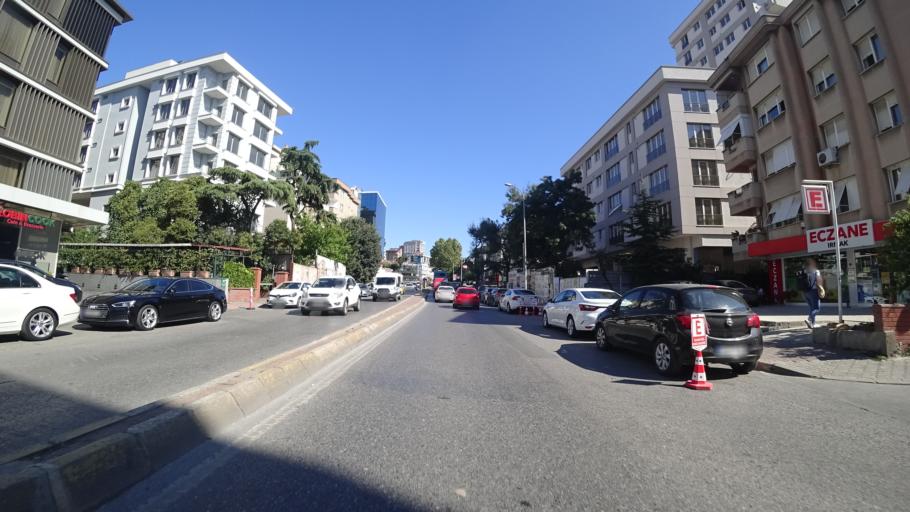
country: TR
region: Istanbul
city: UEskuedar
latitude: 40.9851
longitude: 29.0381
